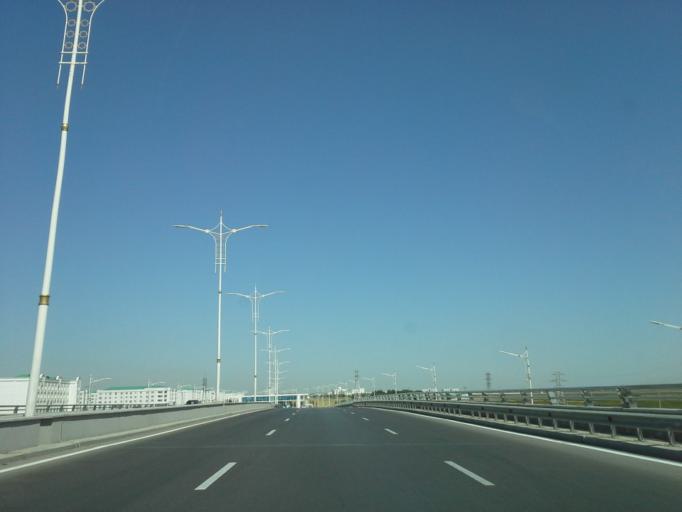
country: TM
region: Ahal
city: Ashgabat
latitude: 37.9777
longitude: 58.3425
